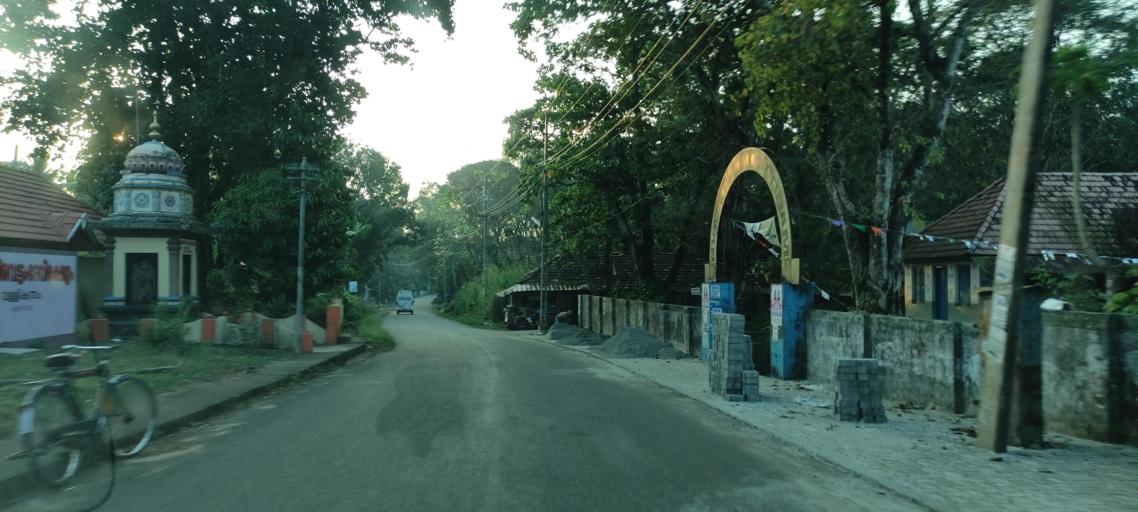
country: IN
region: Kerala
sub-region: Alappuzha
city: Kattanam
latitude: 9.1507
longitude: 76.5790
